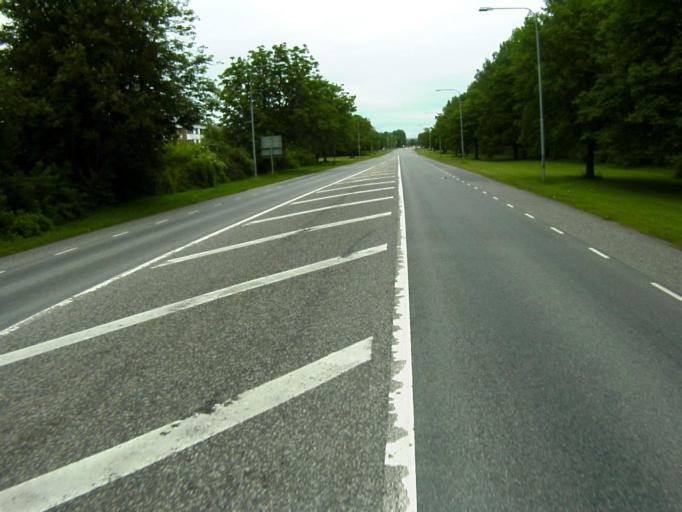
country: SE
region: Skane
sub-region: Kristianstads Kommun
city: Kristianstad
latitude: 56.0502
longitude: 14.1593
